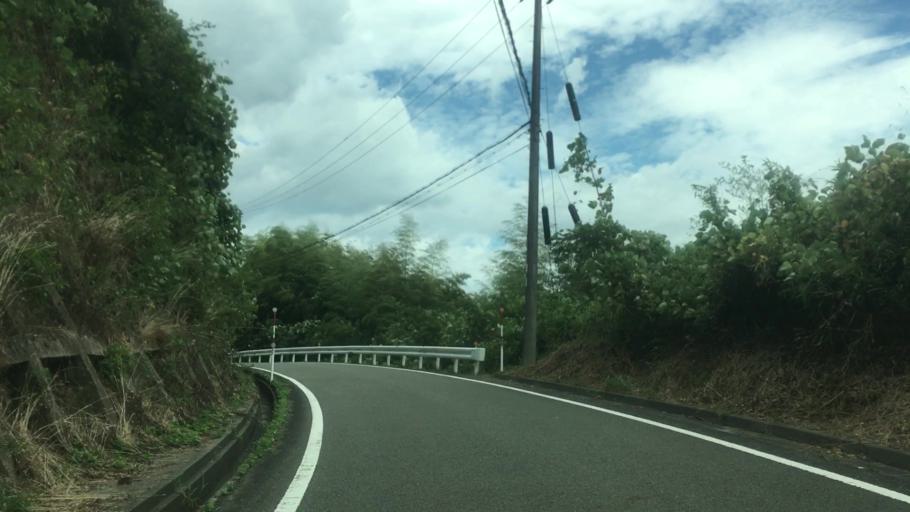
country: JP
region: Hyogo
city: Toyooka
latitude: 35.5847
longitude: 134.7993
